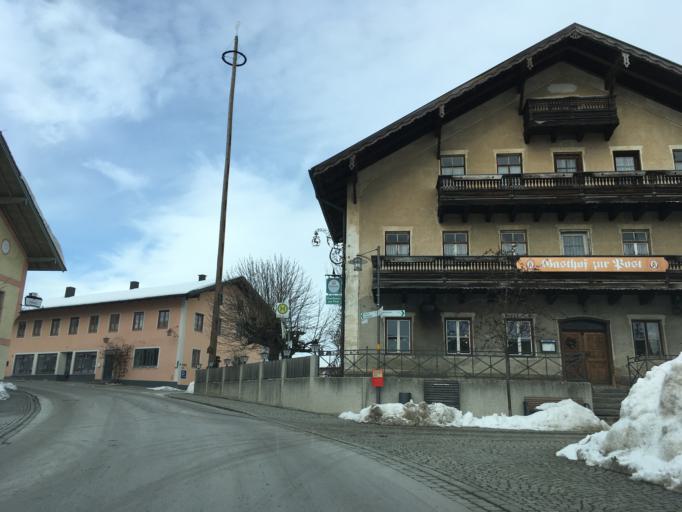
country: DE
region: Bavaria
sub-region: Upper Bavaria
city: Schnaitsee
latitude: 48.0710
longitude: 12.3707
